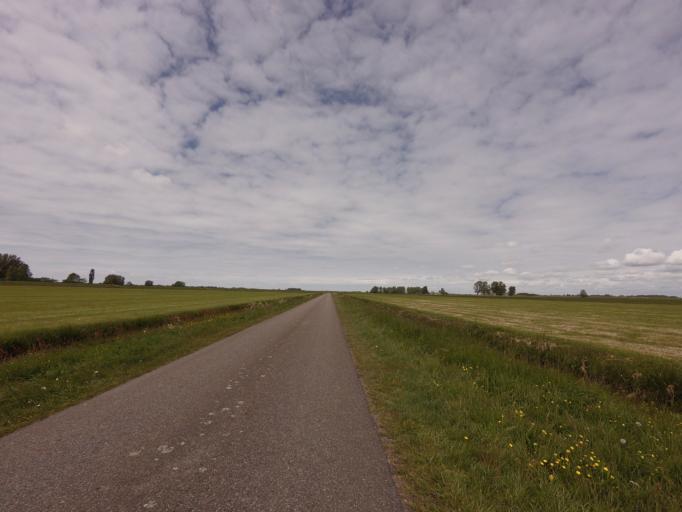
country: NL
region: Friesland
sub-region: Sudwest Fryslan
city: Koudum
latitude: 52.9060
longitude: 5.5029
